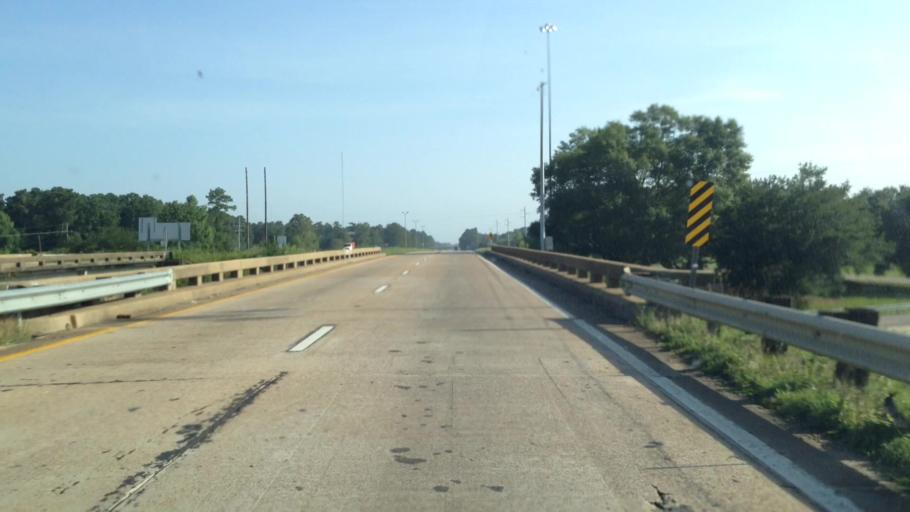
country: US
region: Mississippi
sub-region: Pike County
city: Summit
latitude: 31.2595
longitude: -90.4791
